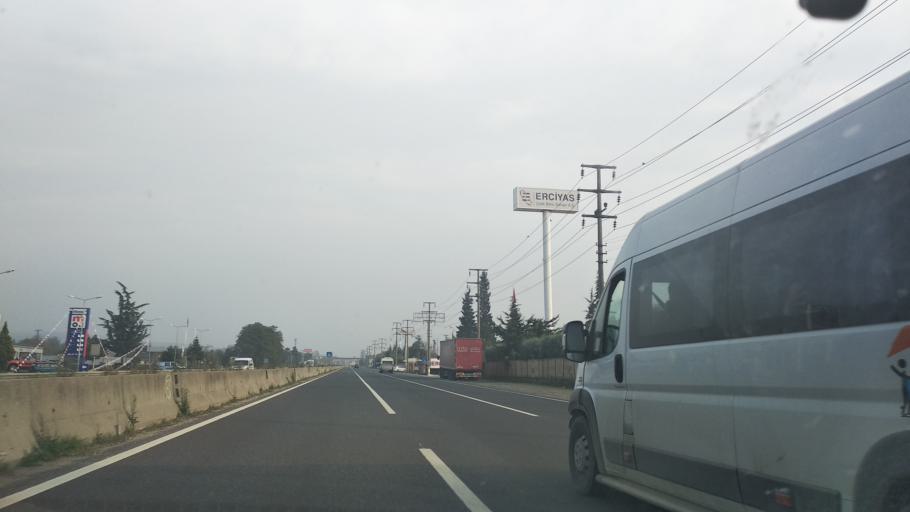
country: TR
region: Duzce
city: Duzce
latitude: 40.8097
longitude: 31.2250
